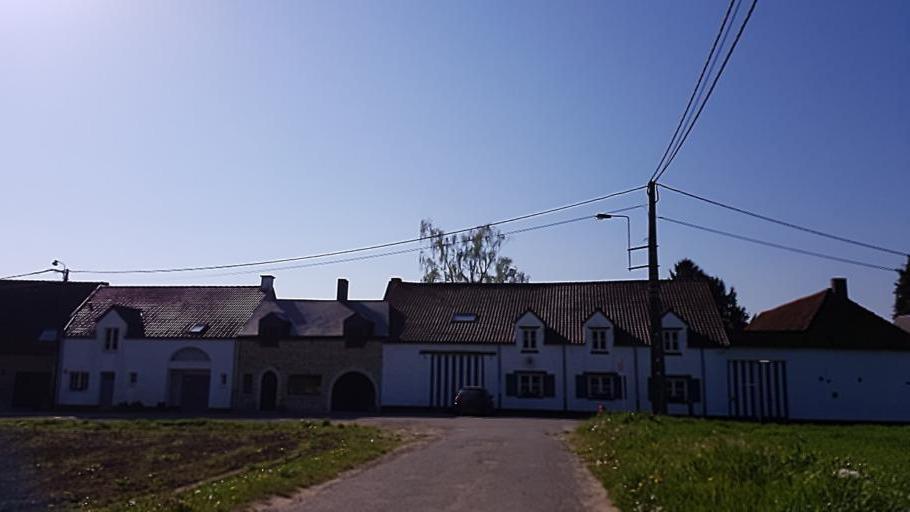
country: BE
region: Wallonia
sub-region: Province du Brabant Wallon
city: Wavre
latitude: 50.7290
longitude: 4.6278
